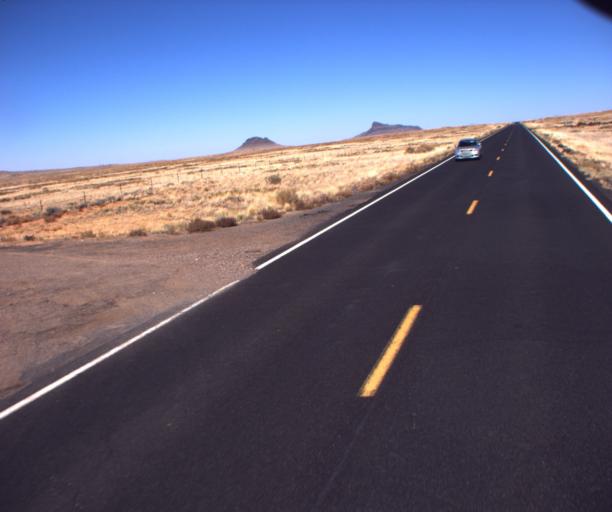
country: US
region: Arizona
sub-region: Navajo County
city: Dilkon
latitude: 35.4014
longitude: -110.4262
